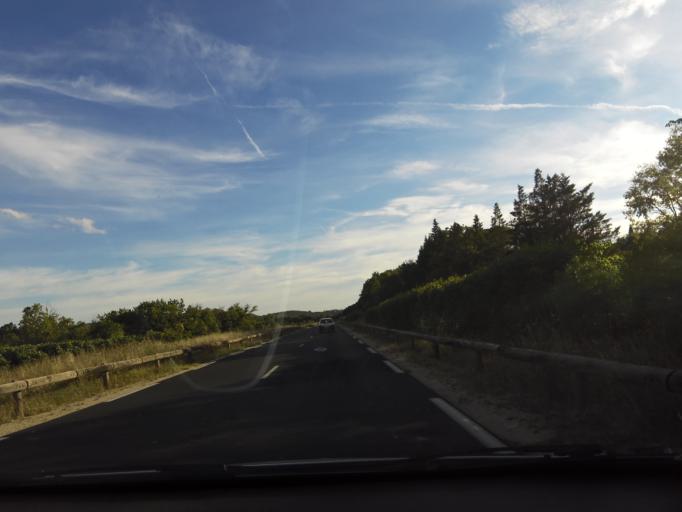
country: FR
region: Languedoc-Roussillon
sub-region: Departement de l'Herault
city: Claret
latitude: 43.8368
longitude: 3.9133
